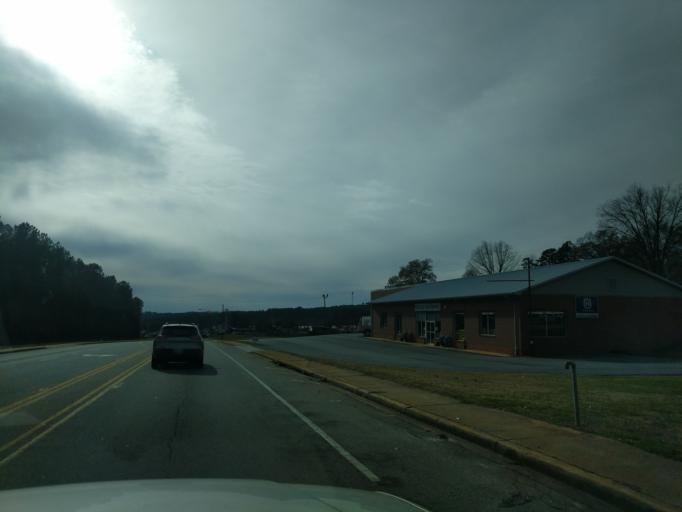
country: US
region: South Carolina
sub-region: Oconee County
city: Walhalla
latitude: 34.7613
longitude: -83.0408
